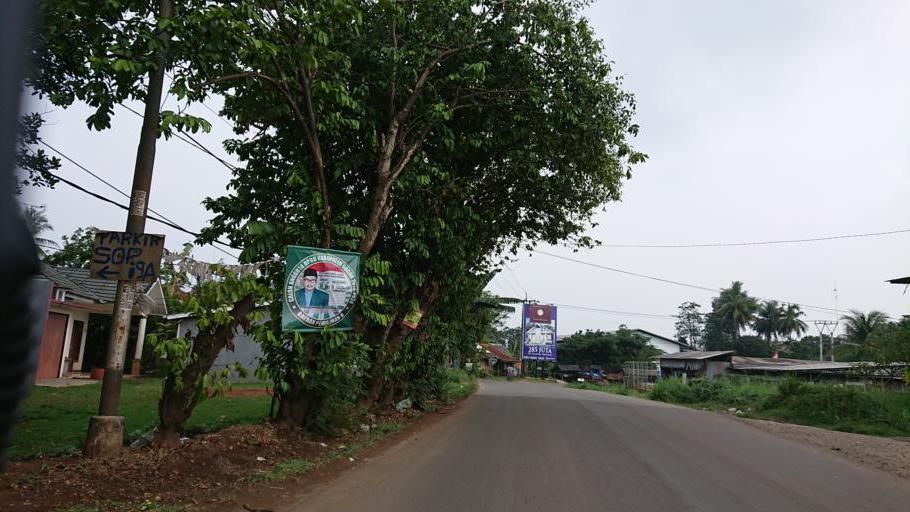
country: ID
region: West Java
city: Parung
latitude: -6.3890
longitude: 106.6832
